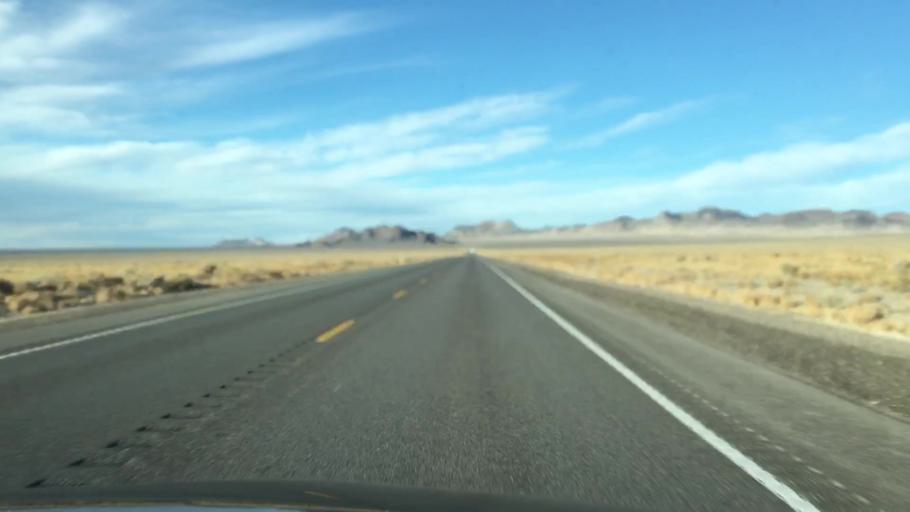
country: US
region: Nevada
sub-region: Esmeralda County
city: Goldfield
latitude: 37.8859
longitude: -117.2426
